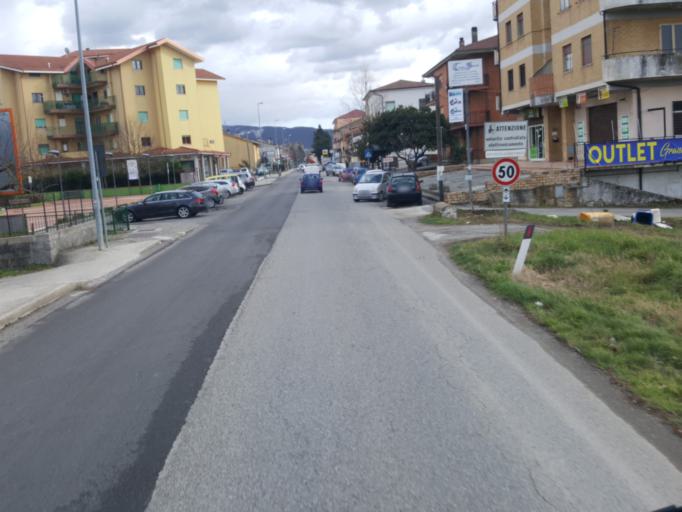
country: IT
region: Calabria
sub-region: Provincia di Cosenza
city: Santo Stefano di Rogliano
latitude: 39.2049
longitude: 16.3117
